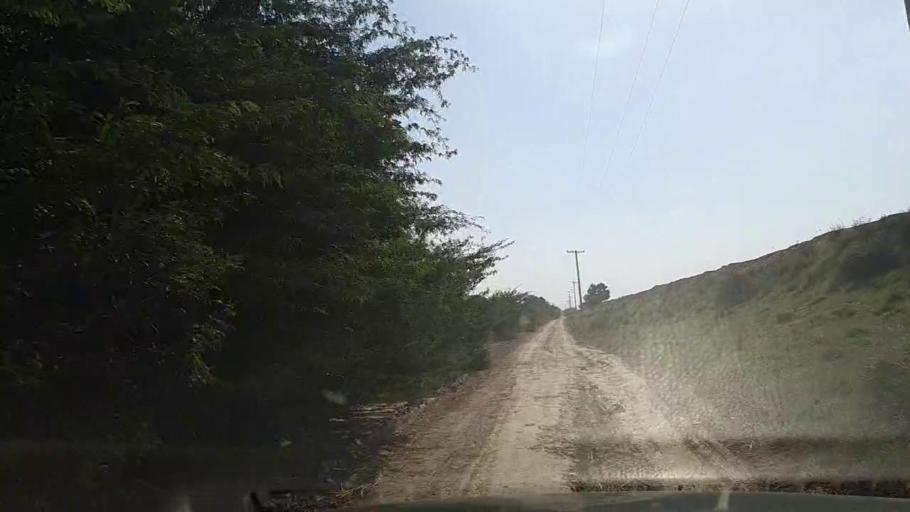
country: PK
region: Sindh
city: Daro Mehar
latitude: 24.7788
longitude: 68.0696
